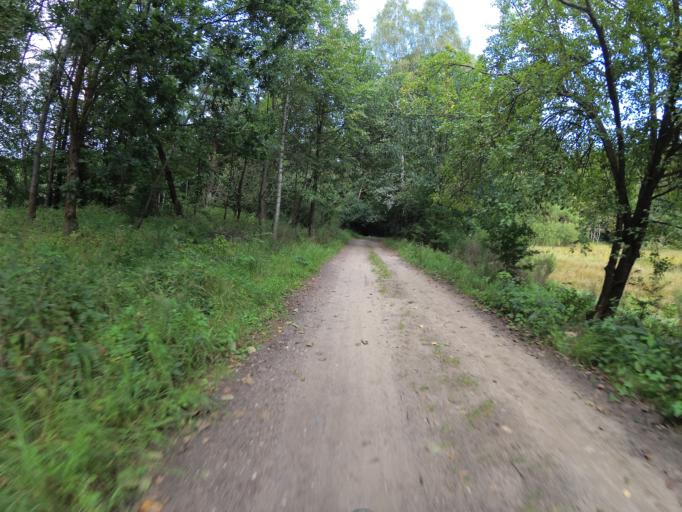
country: PL
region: Pomeranian Voivodeship
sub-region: Gdynia
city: Wielki Kack
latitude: 54.4903
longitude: 18.4684
